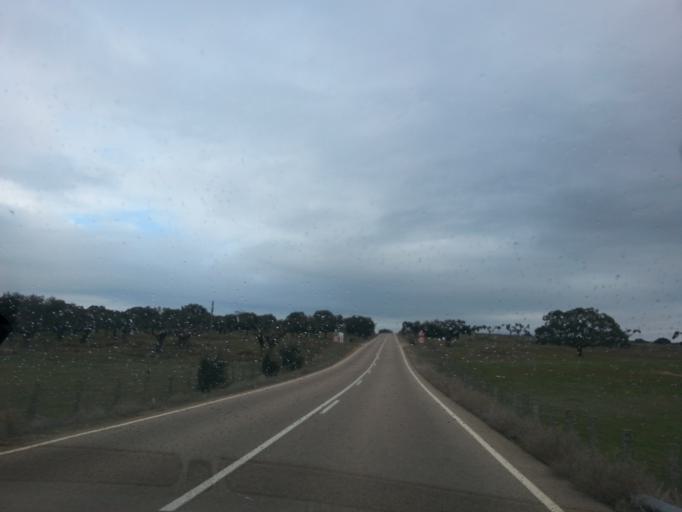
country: ES
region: Castille and Leon
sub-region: Provincia de Salamanca
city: Berrocal de Huebra
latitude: 40.7040
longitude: -6.0127
